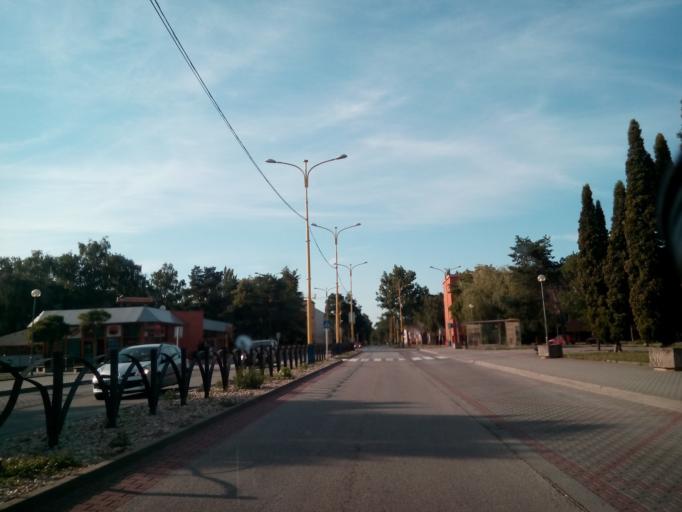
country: SK
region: Kosicky
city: Kosice
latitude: 48.6333
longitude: 21.1723
